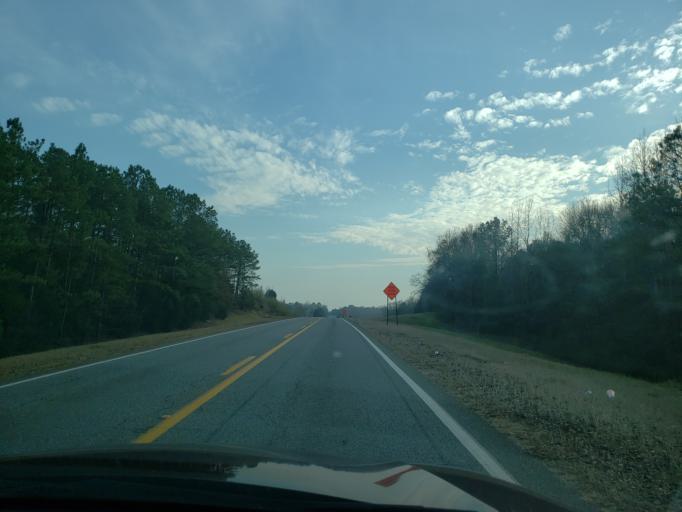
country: US
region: Alabama
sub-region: Hale County
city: Moundville
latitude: 32.9298
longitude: -87.6353
